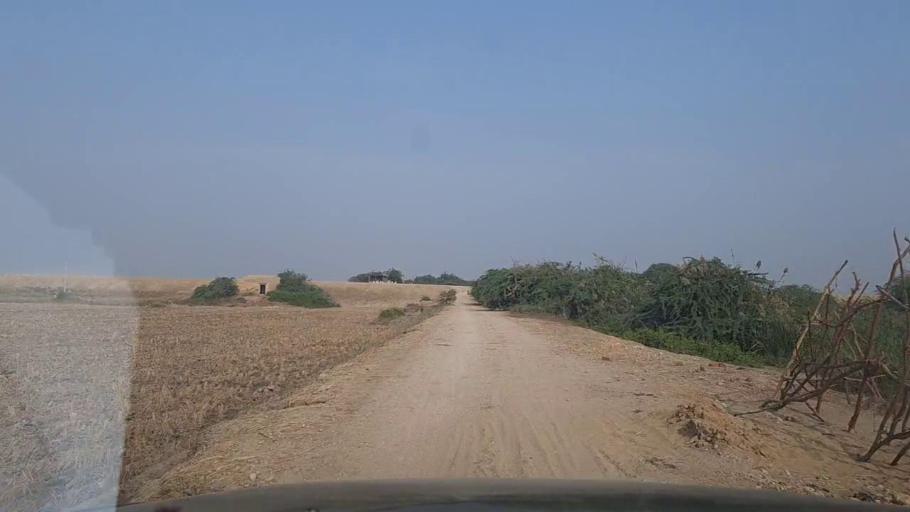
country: PK
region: Sindh
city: Bulri
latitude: 24.9426
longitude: 68.2817
